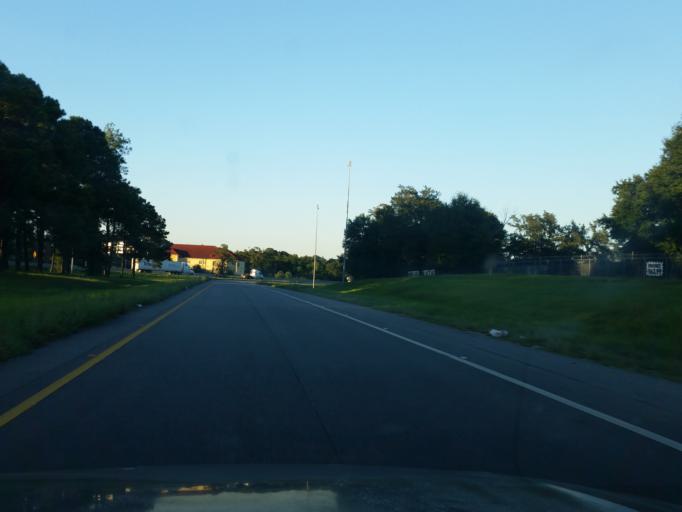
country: US
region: Alabama
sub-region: Mobile County
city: Tillmans Corner
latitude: 30.5807
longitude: -88.1676
